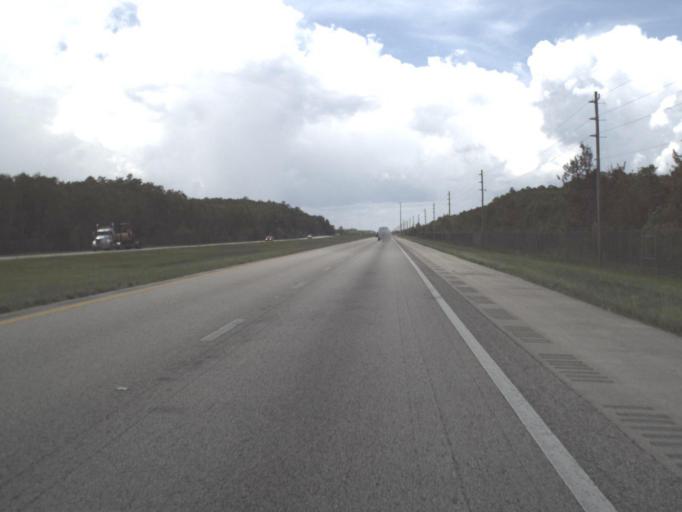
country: US
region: Florida
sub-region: Collier County
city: Immokalee
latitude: 26.1677
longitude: -81.1597
